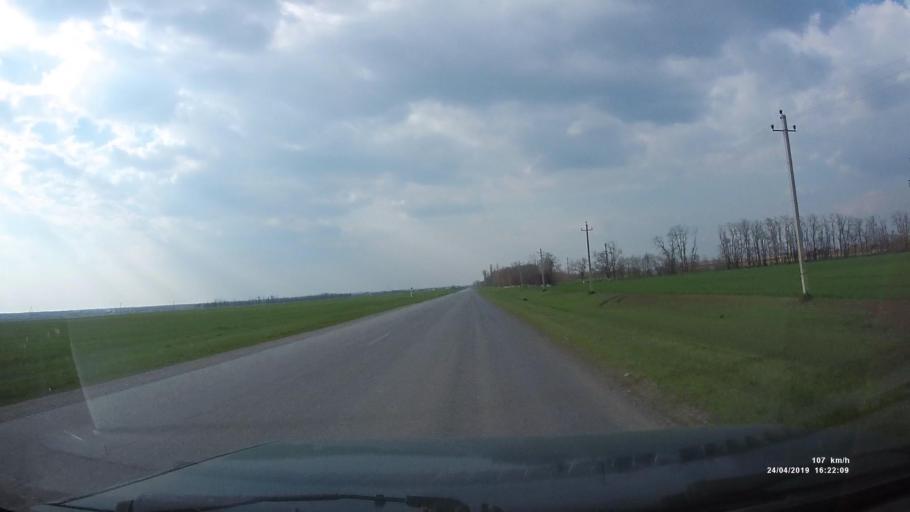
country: RU
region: Rostov
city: Orlovskiy
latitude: 46.8148
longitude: 42.0594
